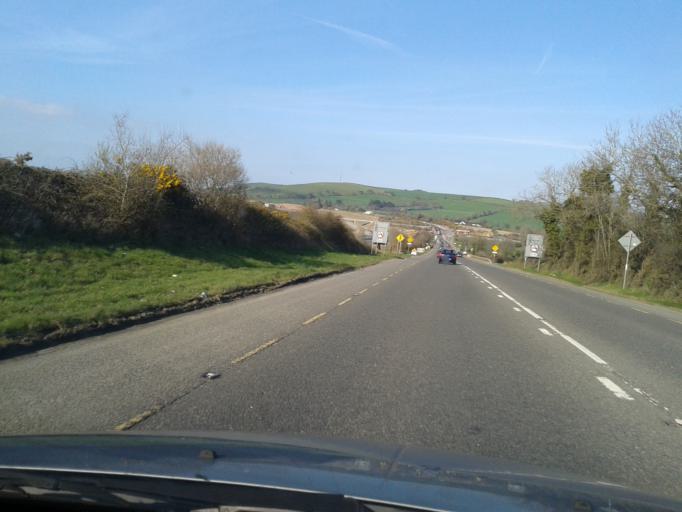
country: IE
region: Leinster
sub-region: Wicklow
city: Rathnew
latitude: 52.9455
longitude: -6.1038
